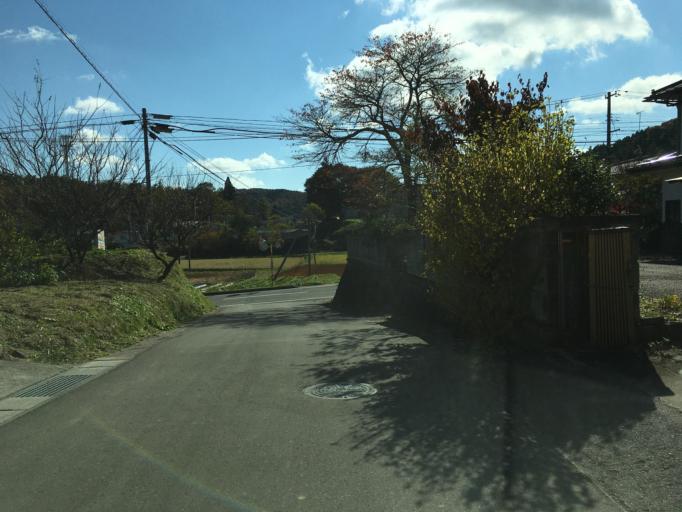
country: JP
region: Fukushima
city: Ishikawa
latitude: 37.2384
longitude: 140.5633
